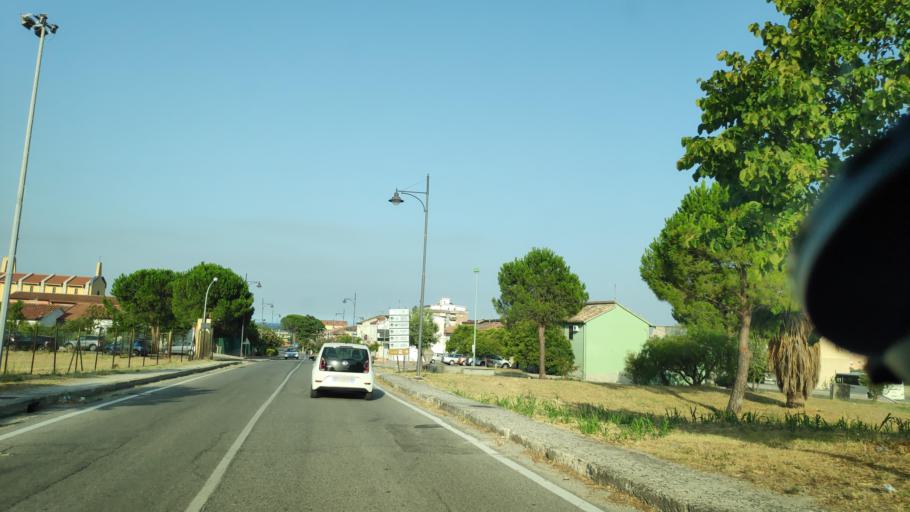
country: IT
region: Calabria
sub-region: Provincia di Catanzaro
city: Sant'Andrea Ionio Marina
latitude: 38.6193
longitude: 16.5492
